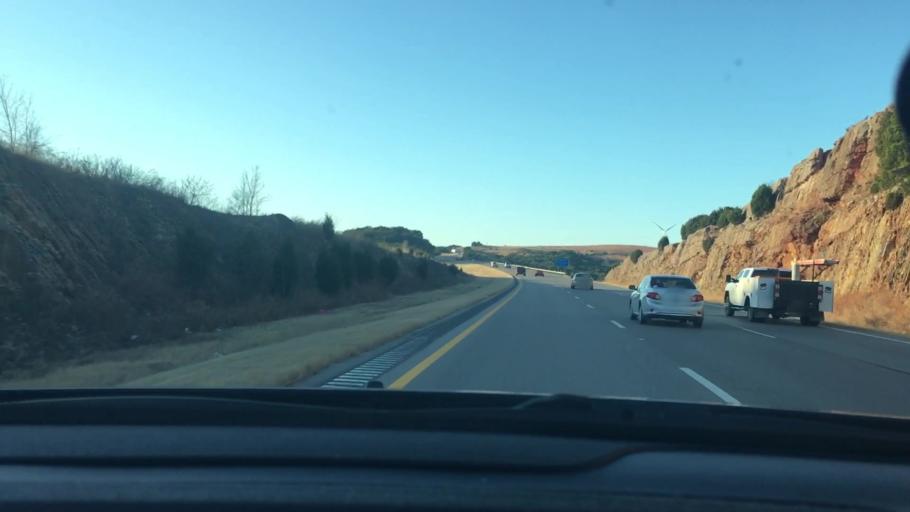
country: US
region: Oklahoma
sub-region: Murray County
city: Davis
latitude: 34.4336
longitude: -97.1311
